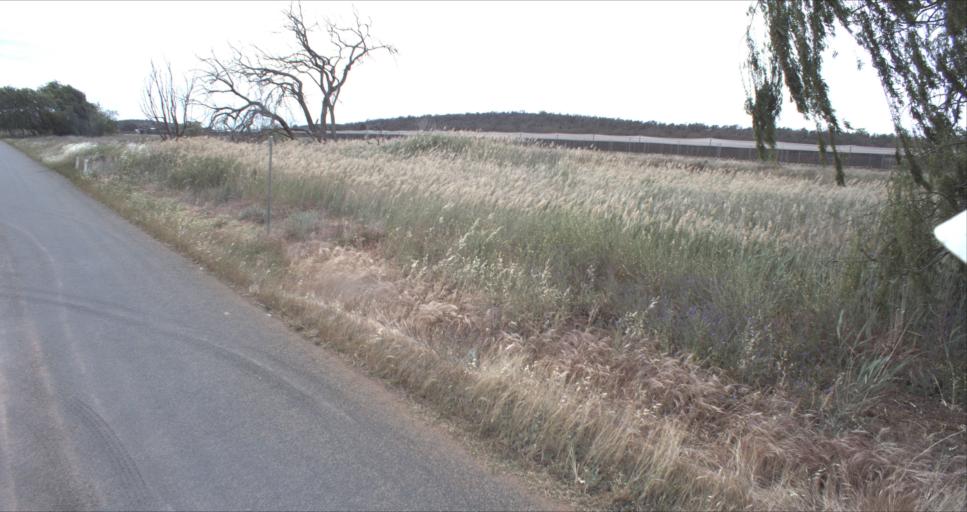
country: AU
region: New South Wales
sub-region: Leeton
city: Leeton
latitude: -34.4283
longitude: 146.3779
